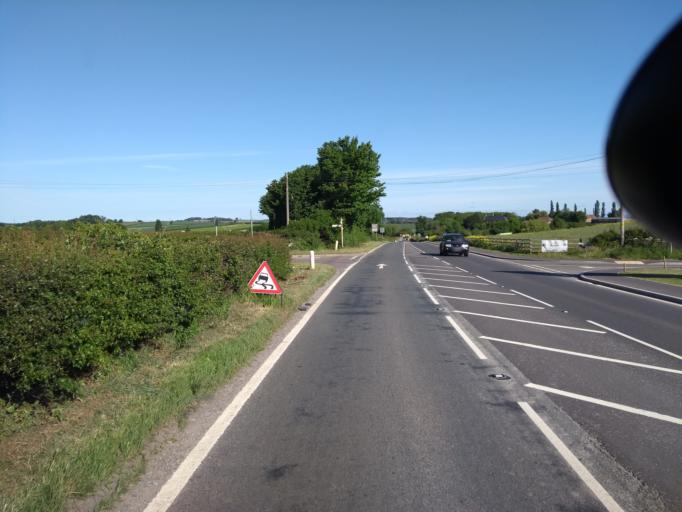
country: GB
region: England
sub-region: Somerset
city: Bridgwater
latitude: 51.1315
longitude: -3.0413
